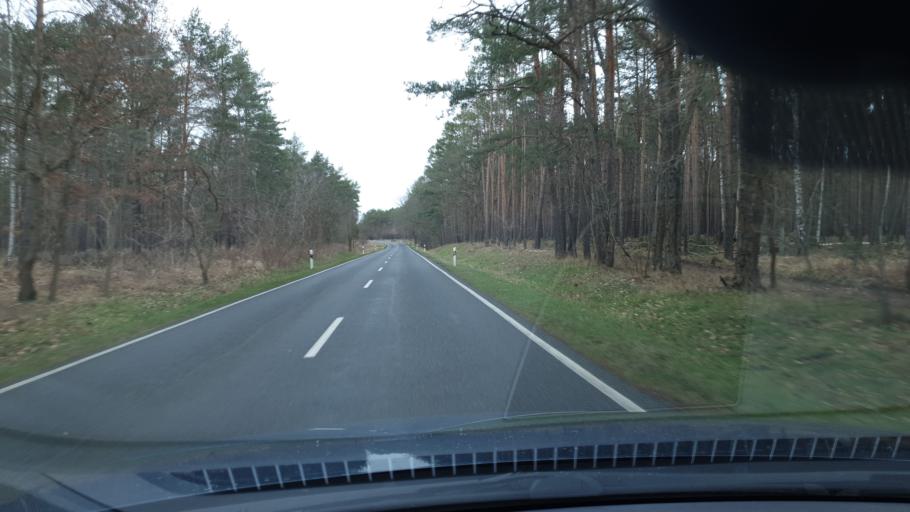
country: DE
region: Saxony-Anhalt
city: Radis
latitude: 51.7690
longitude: 12.4958
